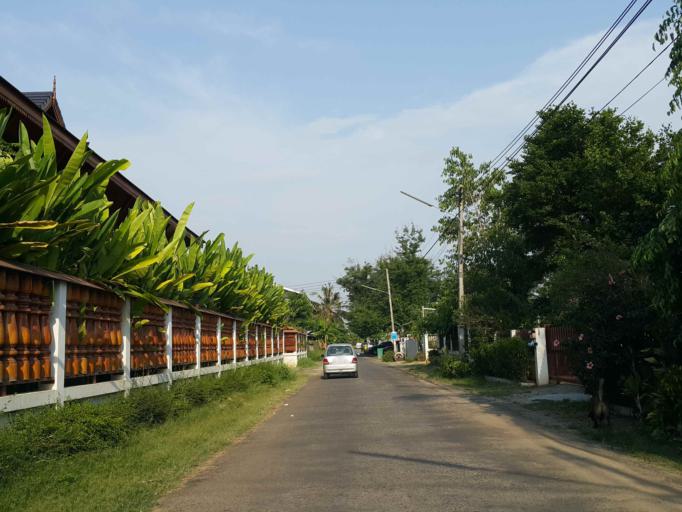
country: TH
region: Chiang Mai
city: Chiang Mai
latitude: 18.7749
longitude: 99.0233
